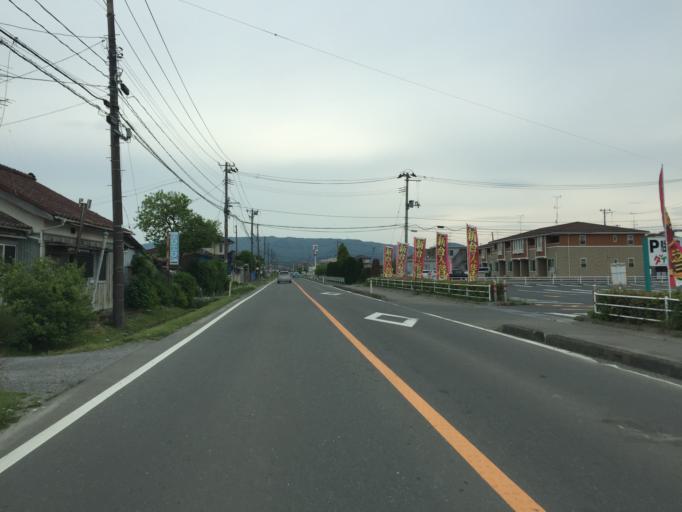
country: JP
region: Miyagi
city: Marumori
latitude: 37.7925
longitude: 140.9360
